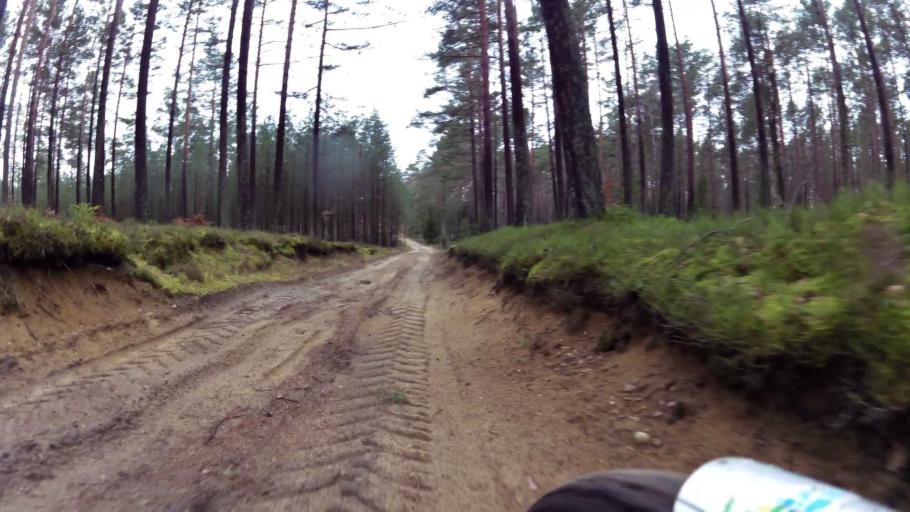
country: PL
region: Pomeranian Voivodeship
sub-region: Powiat bytowski
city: Borzytuchom
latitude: 54.2644
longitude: 17.3553
